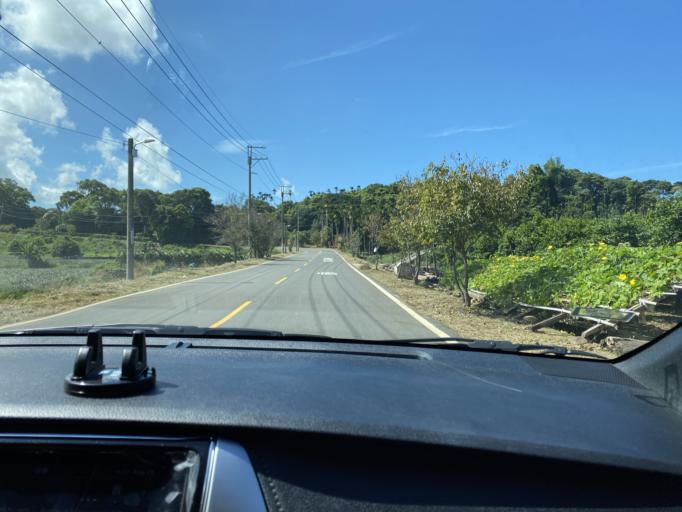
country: TW
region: Taiwan
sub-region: Nantou
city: Nantou
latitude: 23.8669
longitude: 120.6323
